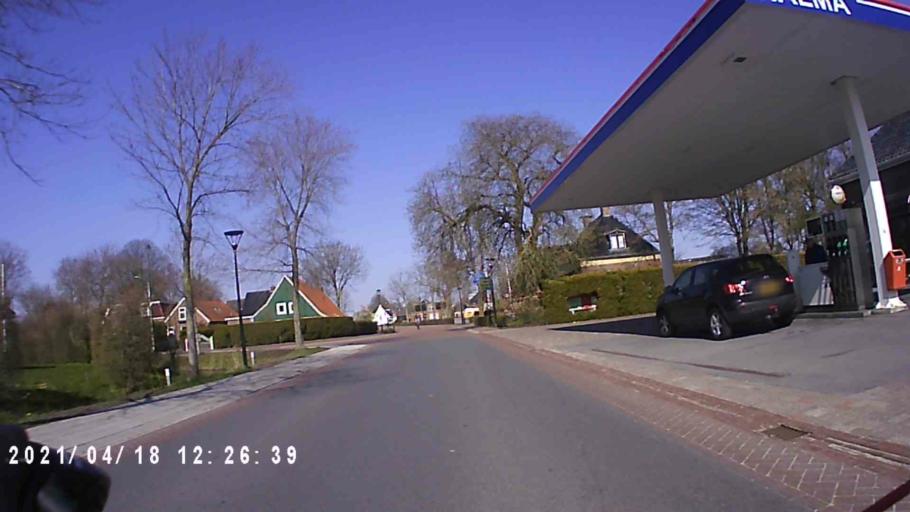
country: NL
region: Friesland
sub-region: Gemeente Dongeradeel
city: Anjum
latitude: 53.3301
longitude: 6.1047
